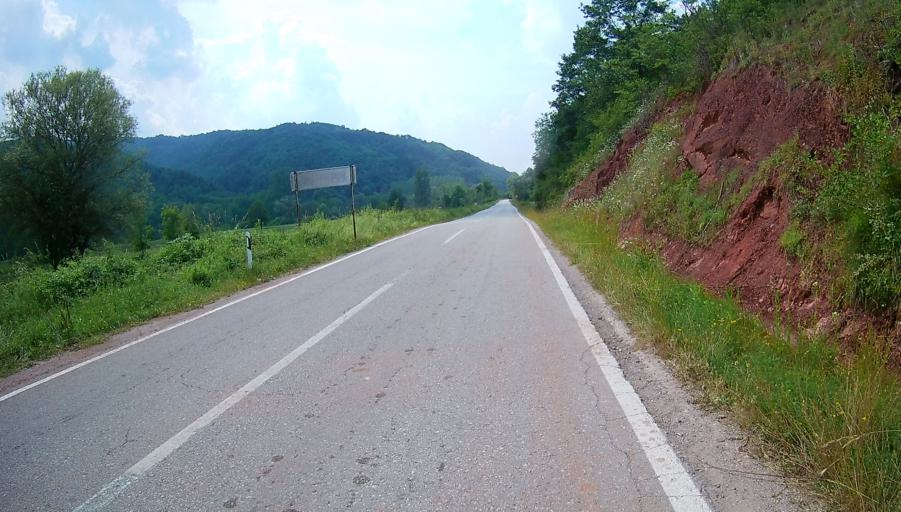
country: RS
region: Central Serbia
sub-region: Nisavski Okrug
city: Gadzin Han
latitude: 43.1654
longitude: 22.0946
